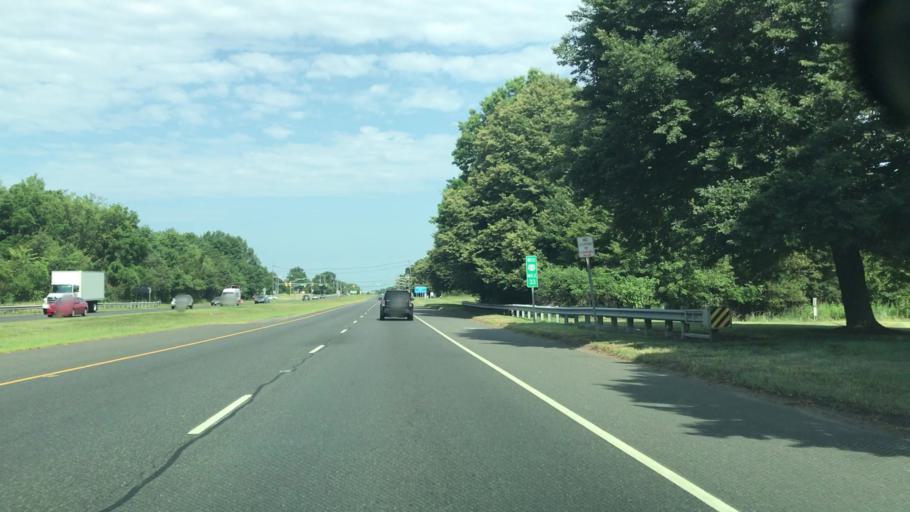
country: US
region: New Jersey
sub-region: Somerset County
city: Bridgewater
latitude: 40.5874
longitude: -74.6368
